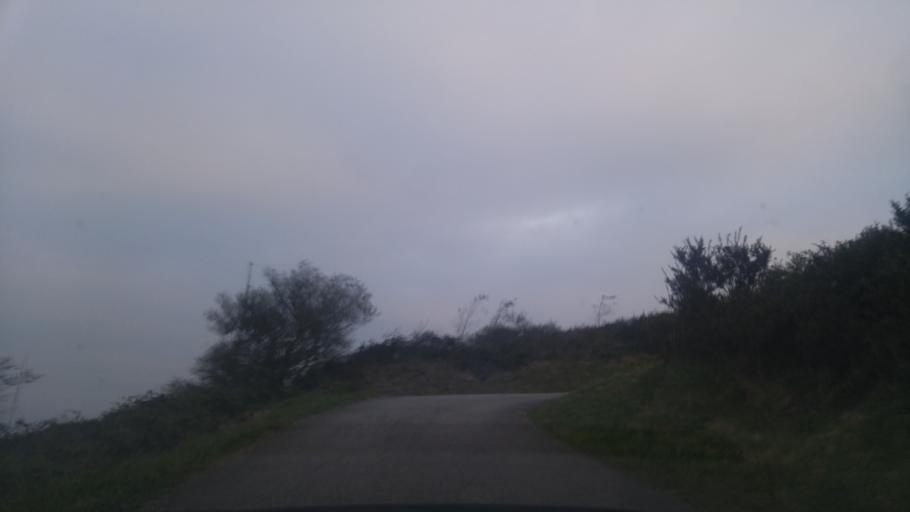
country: ES
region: Asturias
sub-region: Province of Asturias
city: Oviedo
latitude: 43.3853
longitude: -5.8643
